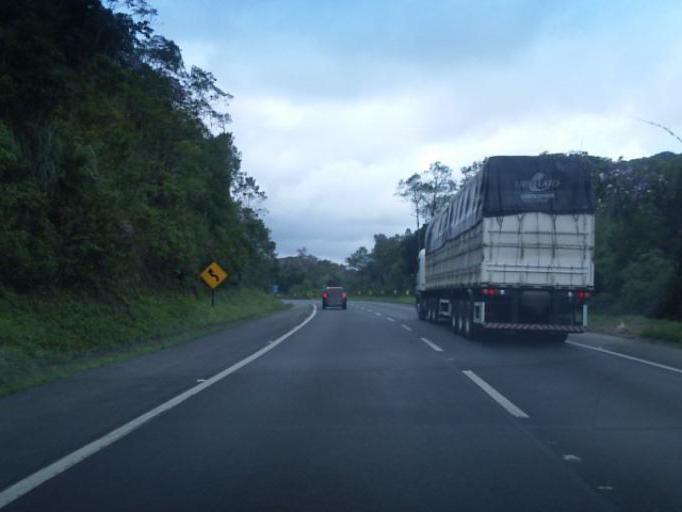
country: BR
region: Sao Paulo
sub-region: Cajati
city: Cajati
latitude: -24.9636
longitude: -48.4273
